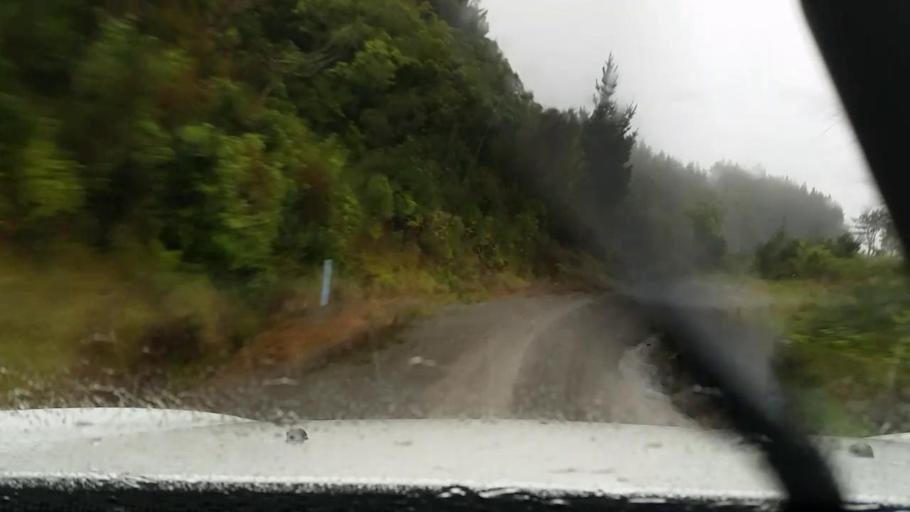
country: NZ
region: Wellington
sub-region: Masterton District
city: Masterton
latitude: -41.1905
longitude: 175.8161
